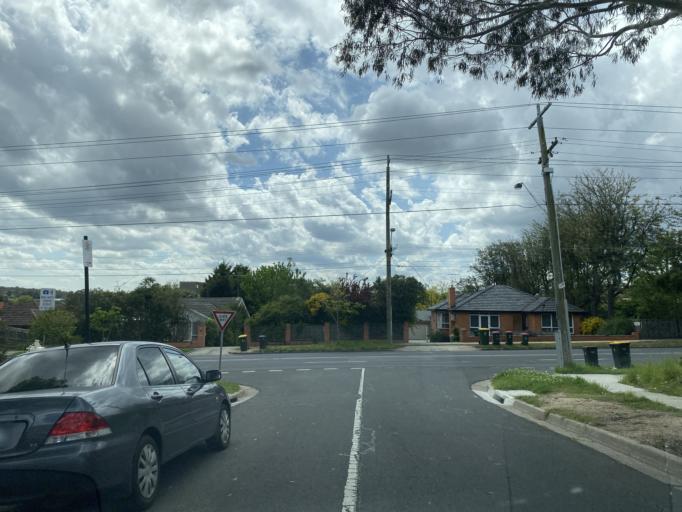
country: AU
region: Victoria
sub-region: Whitehorse
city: Burwood
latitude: -37.8561
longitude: 145.1164
